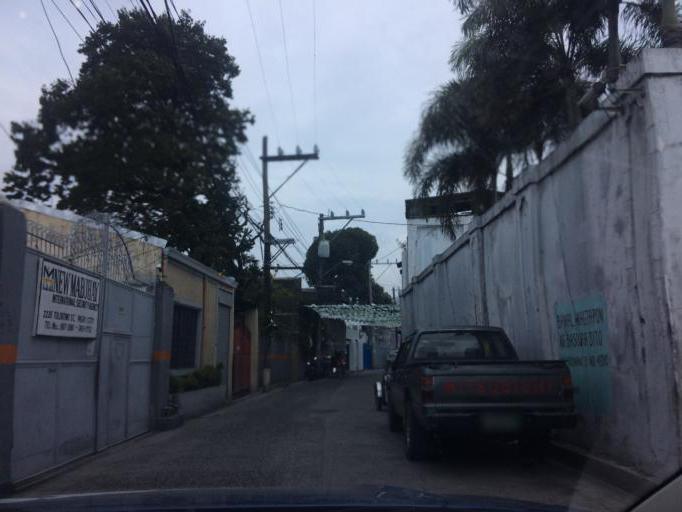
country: PH
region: Metro Manila
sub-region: Makati City
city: Makati City
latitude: 14.5478
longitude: 121.0050
